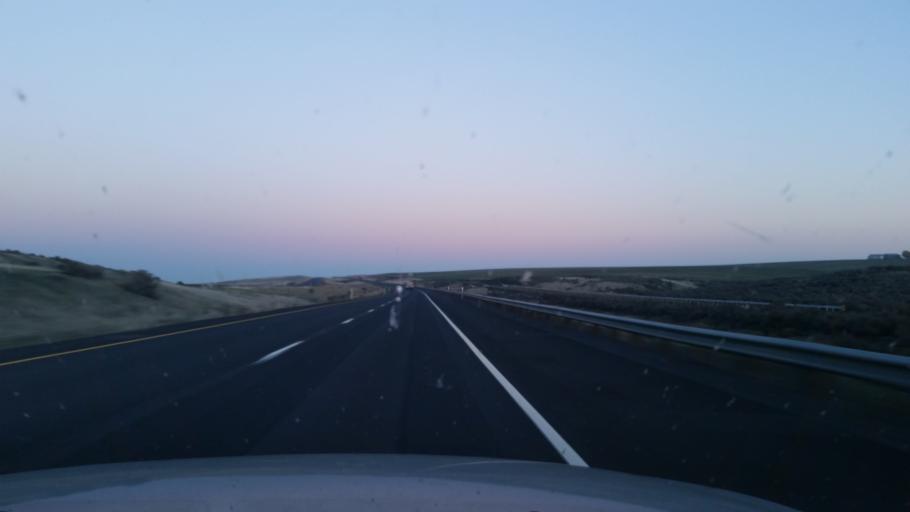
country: US
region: Washington
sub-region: Adams County
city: Ritzville
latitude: 47.1106
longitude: -118.5588
